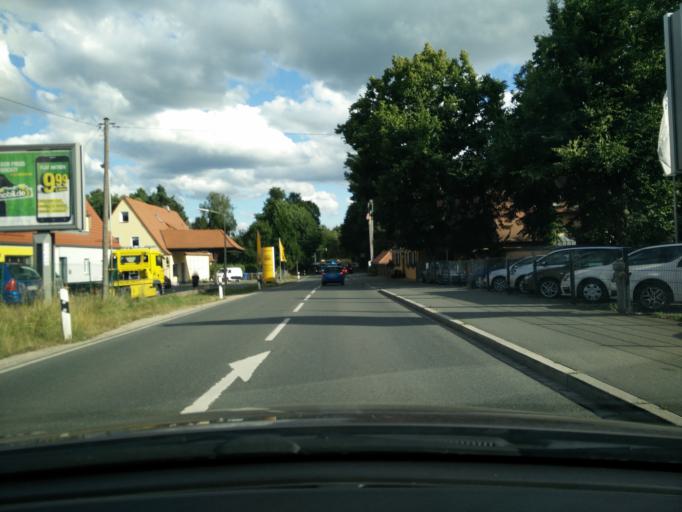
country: DE
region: Bavaria
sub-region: Regierungsbezirk Mittelfranken
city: Wendelstein
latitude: 49.4084
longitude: 11.1626
